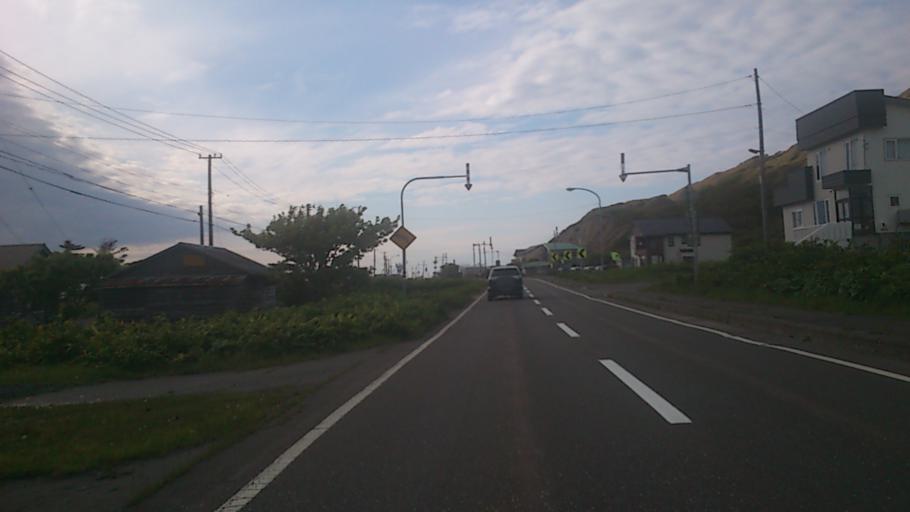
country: JP
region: Hokkaido
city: Wakkanai
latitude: 45.3843
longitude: 141.6450
